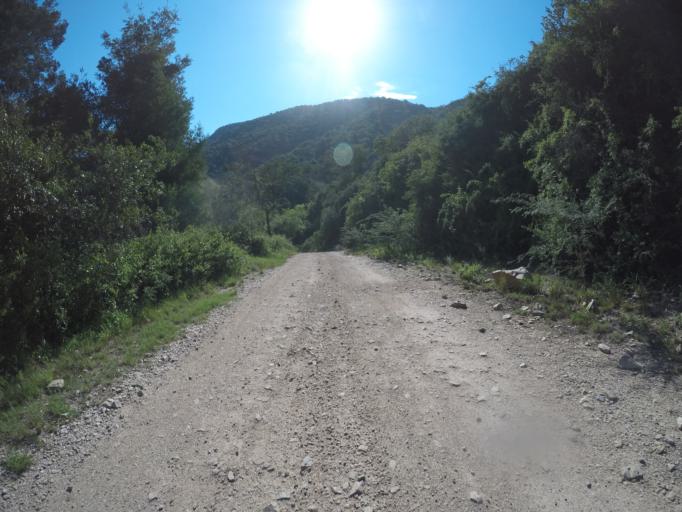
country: ZA
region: Eastern Cape
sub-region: Cacadu District Municipality
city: Kareedouw
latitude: -33.6531
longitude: 24.4191
